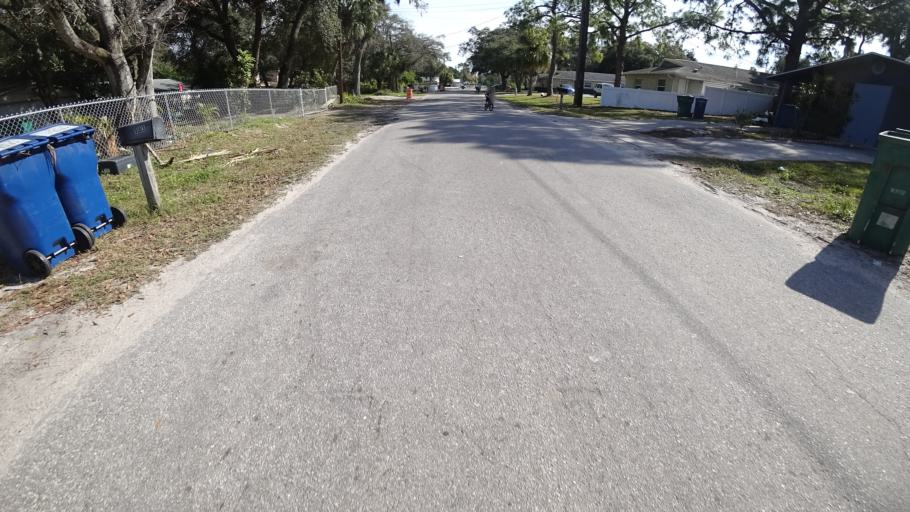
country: US
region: Florida
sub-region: Manatee County
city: Bayshore Gardens
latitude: 27.4337
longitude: -82.5707
